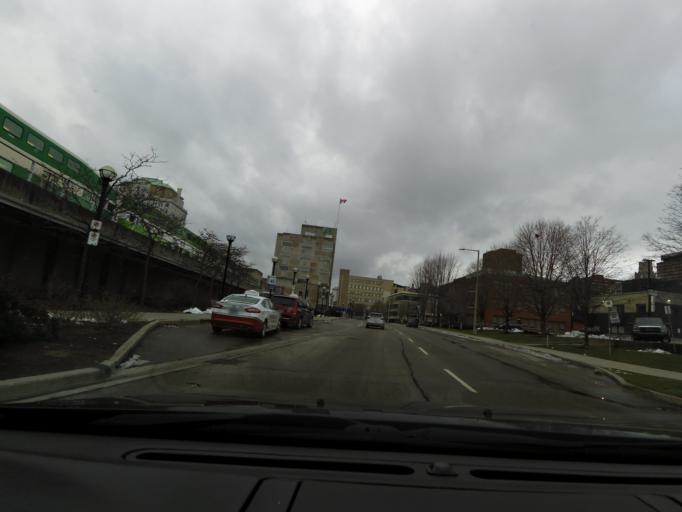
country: CA
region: Ontario
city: Hamilton
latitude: 43.2531
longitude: -79.8679
